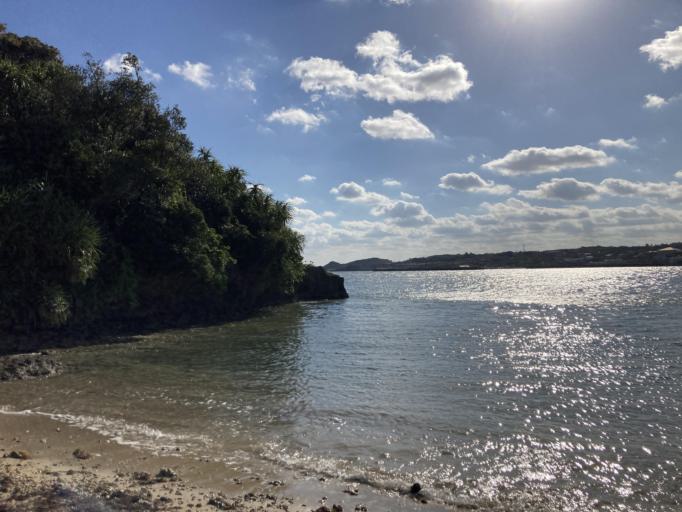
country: JP
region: Okinawa
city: Katsuren-haebaru
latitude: 26.3147
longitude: 127.9284
